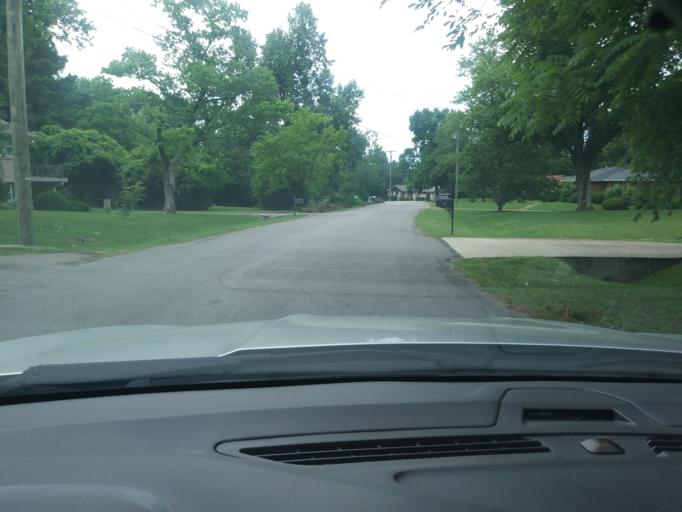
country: US
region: Tennessee
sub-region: Davidson County
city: Nashville
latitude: 36.1297
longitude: -86.7211
